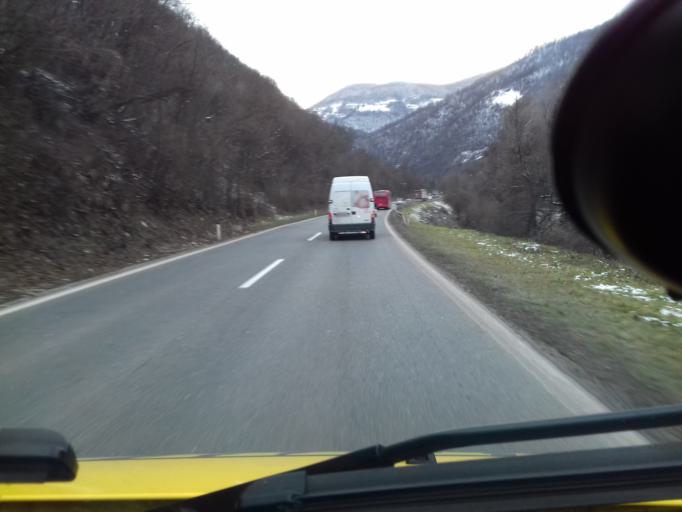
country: BA
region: Federation of Bosnia and Herzegovina
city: Lokvine
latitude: 44.2659
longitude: 17.8809
